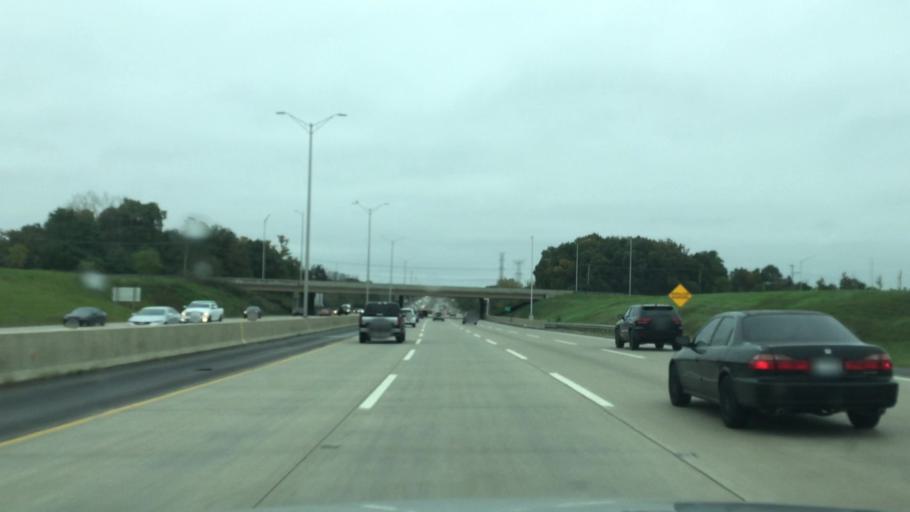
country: US
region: Illinois
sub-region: Lake County
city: Gurnee
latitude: 42.3593
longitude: -87.9363
